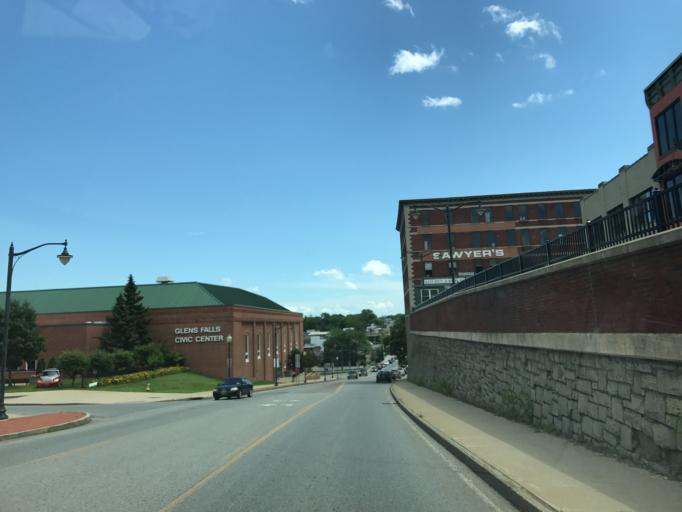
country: US
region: New York
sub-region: Warren County
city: Glens Falls
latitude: 43.3086
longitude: -73.6433
